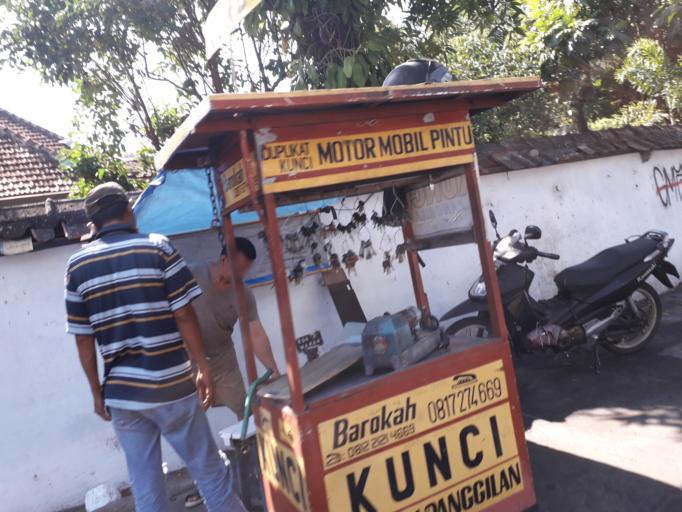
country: ID
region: Daerah Istimewa Yogyakarta
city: Yogyakarta
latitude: -7.7720
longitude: 110.3761
